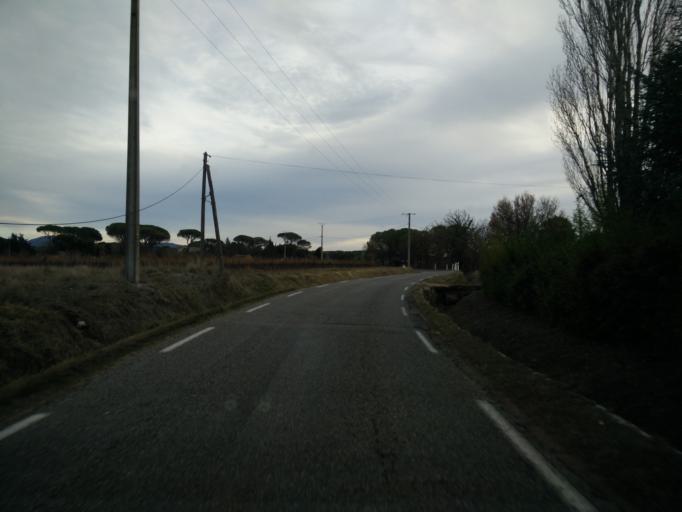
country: FR
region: Provence-Alpes-Cote d'Azur
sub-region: Departement du Var
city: Vidauban
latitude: 43.3994
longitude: 6.4314
